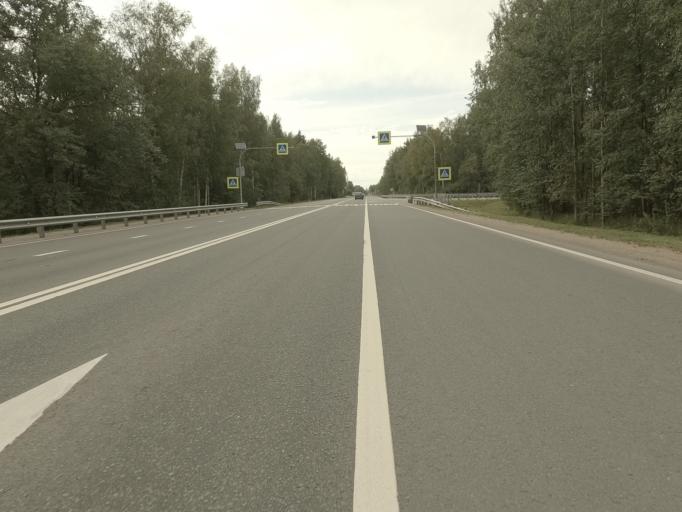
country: RU
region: Leningrad
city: Kirovsk
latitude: 59.8521
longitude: 31.0237
